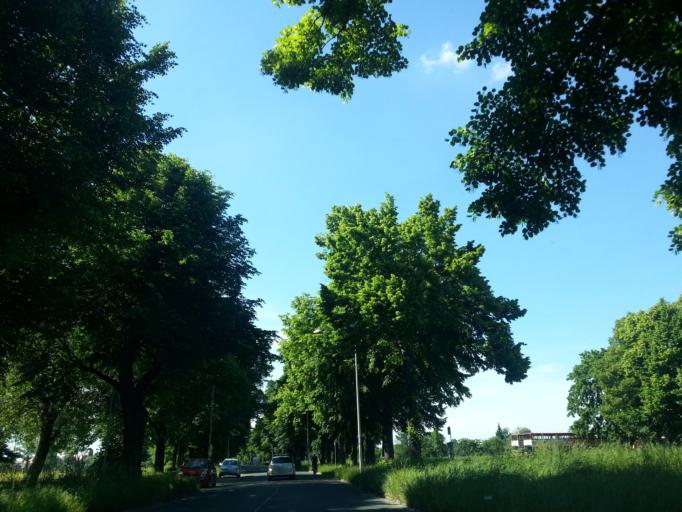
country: DE
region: Saxony
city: Dresden
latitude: 51.0628
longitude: 13.7284
